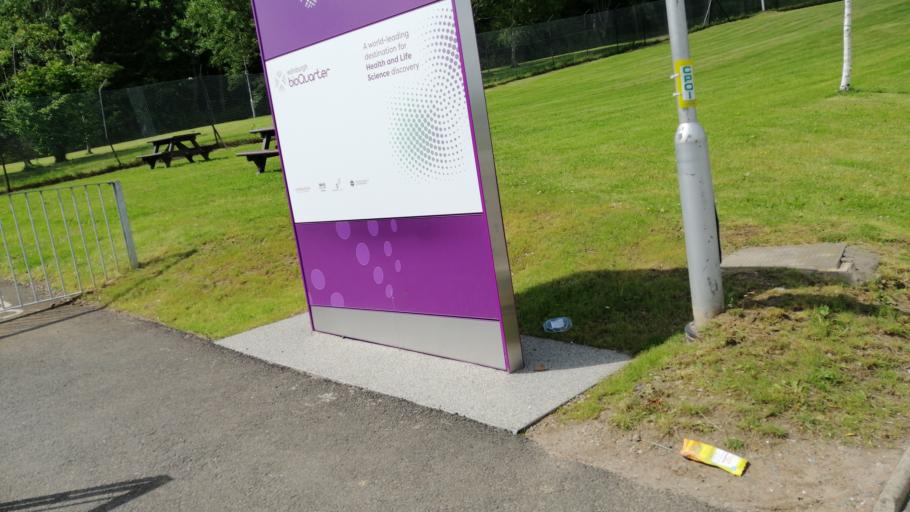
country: GB
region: Scotland
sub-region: West Lothian
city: Seafield
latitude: 55.9226
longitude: -3.1383
